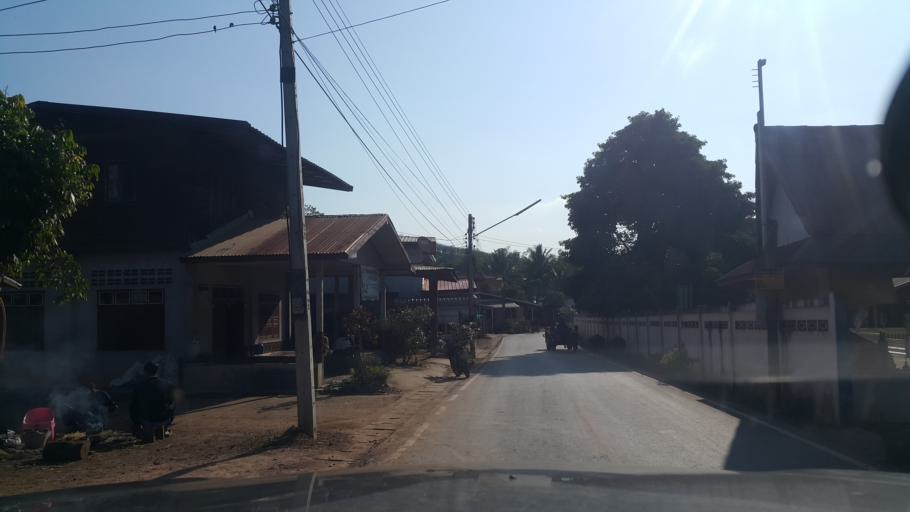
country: TH
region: Loei
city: Chiang Khan
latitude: 17.8047
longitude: 101.6234
